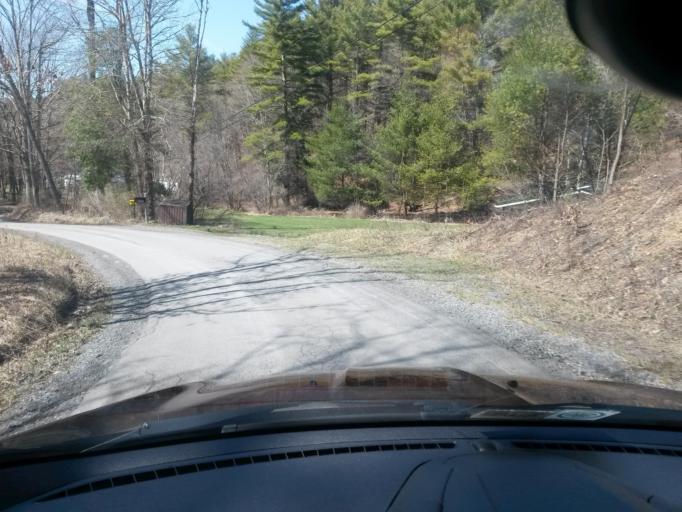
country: US
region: West Virginia
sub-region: Greenbrier County
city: White Sulphur Springs
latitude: 37.6810
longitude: -80.3338
